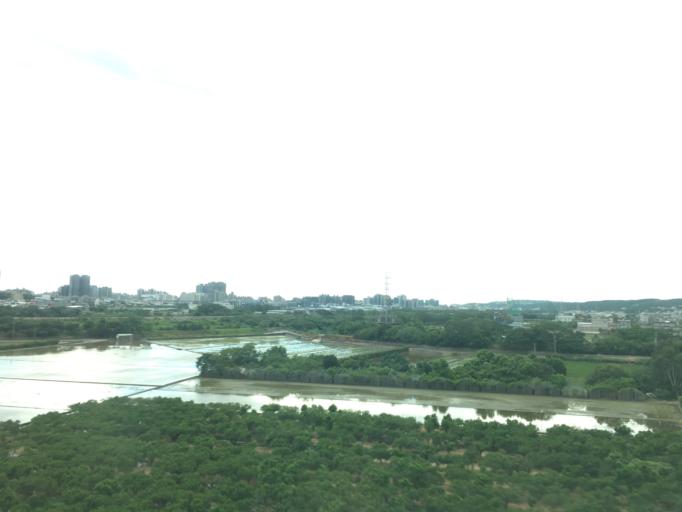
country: TW
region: Taiwan
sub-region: Hsinchu
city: Zhubei
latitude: 24.8326
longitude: 121.0464
